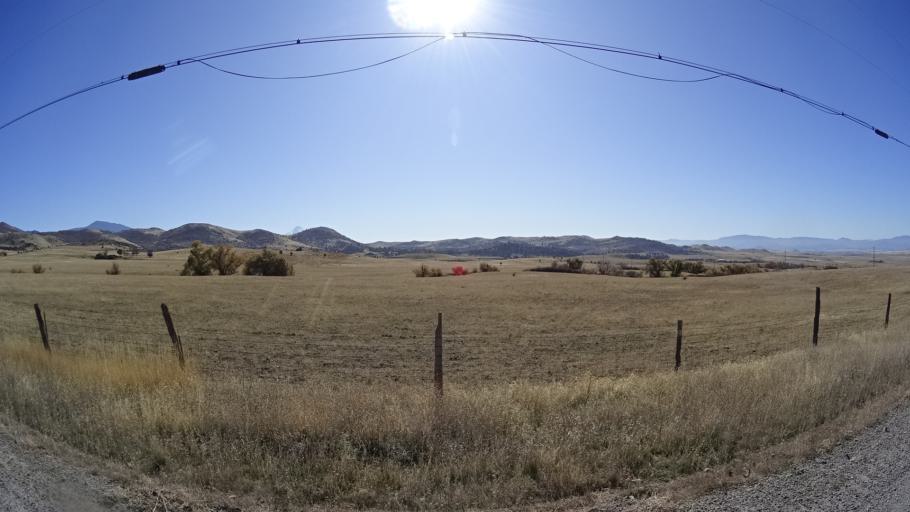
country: US
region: California
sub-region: Siskiyou County
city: Montague
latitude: 41.8299
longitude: -122.3690
